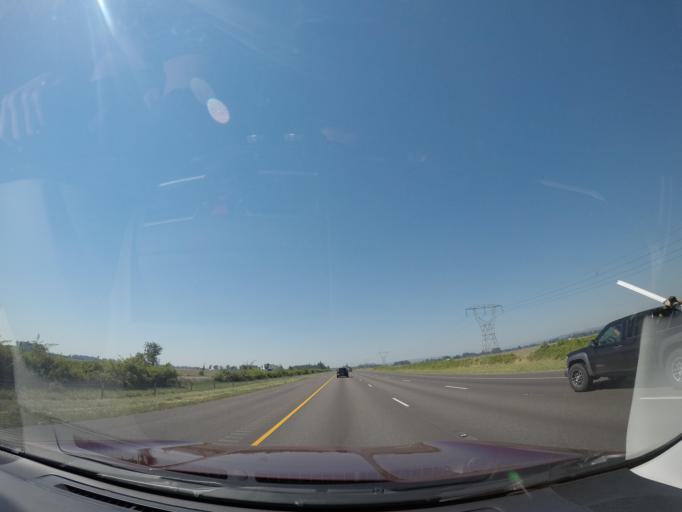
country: US
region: Oregon
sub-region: Marion County
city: Gervais
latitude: 45.0847
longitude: -122.9484
